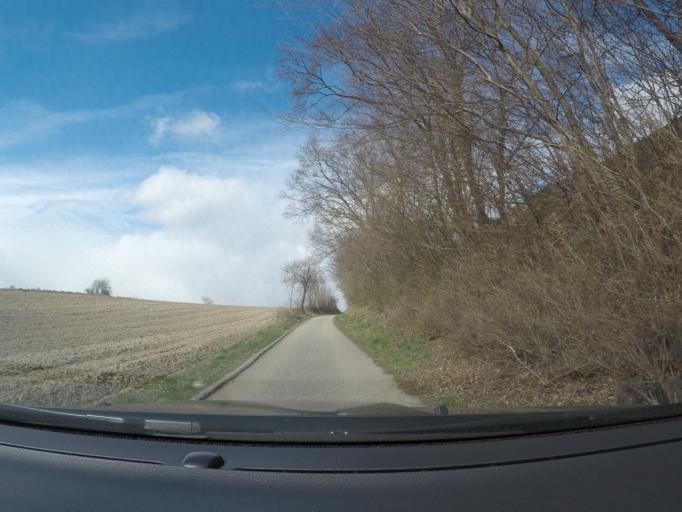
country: AT
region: Lower Austria
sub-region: Politischer Bezirk Neunkirchen
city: Pitten
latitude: 47.7269
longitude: 16.1869
